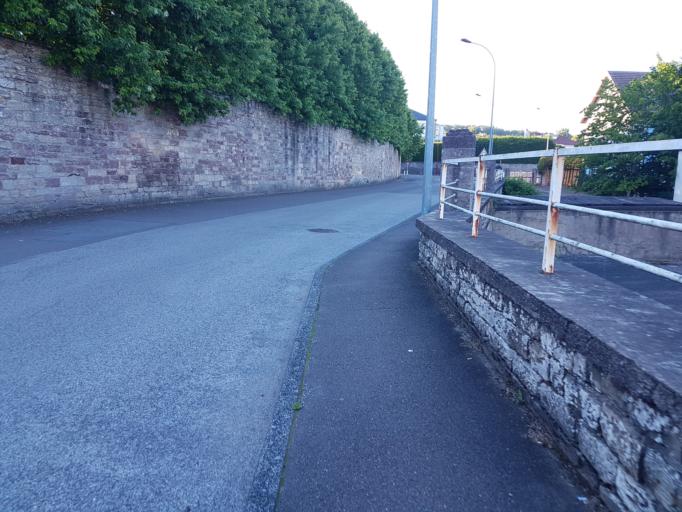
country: FR
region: Franche-Comte
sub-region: Departement de la Haute-Saone
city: Saint-Sauveur
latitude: 47.8160
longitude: 6.3834
